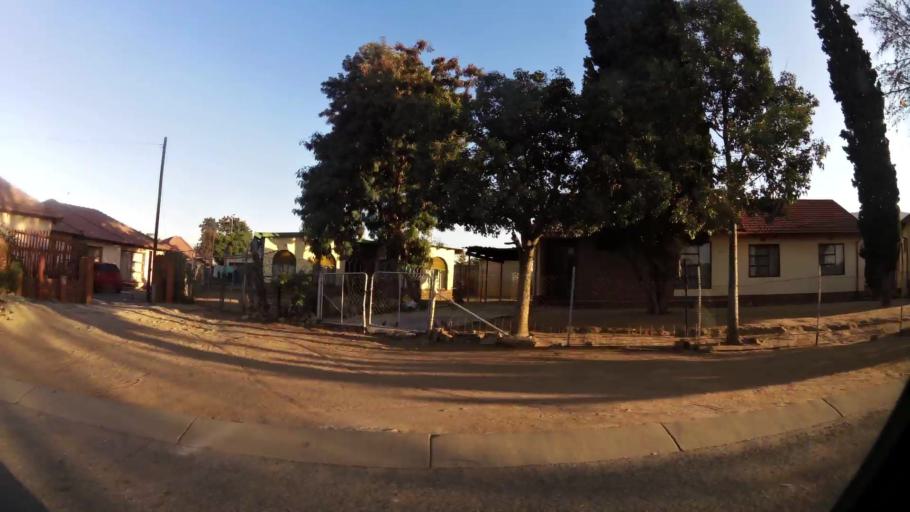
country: ZA
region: North-West
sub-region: Bojanala Platinum District Municipality
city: Rustenburg
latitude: -25.6446
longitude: 27.2099
